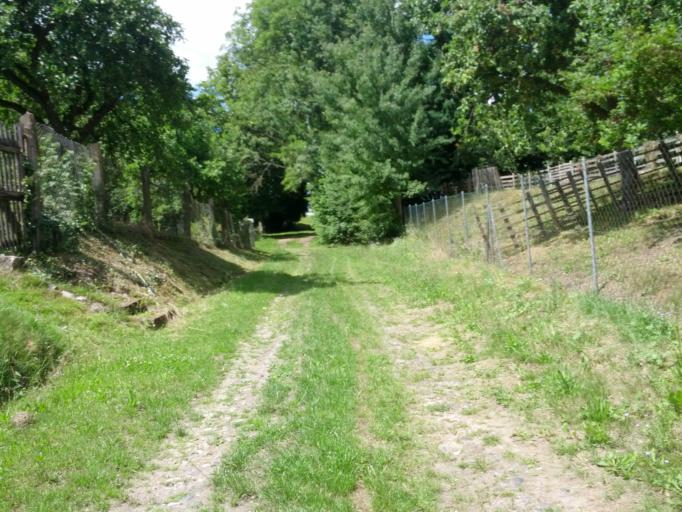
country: DE
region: Thuringia
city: Bischofroda
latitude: 51.0115
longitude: 10.3646
